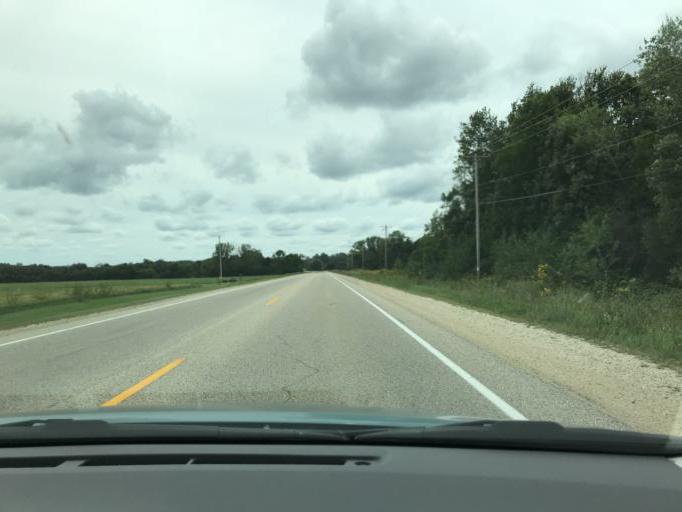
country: US
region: Wisconsin
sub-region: Racine County
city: Bohners Lake
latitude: 42.6359
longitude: -88.2489
